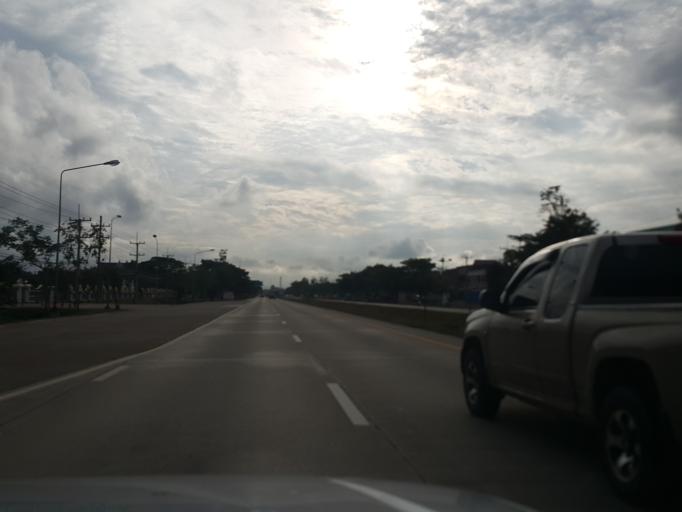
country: TH
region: Lampang
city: Ko Kha
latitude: 18.2092
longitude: 99.4163
